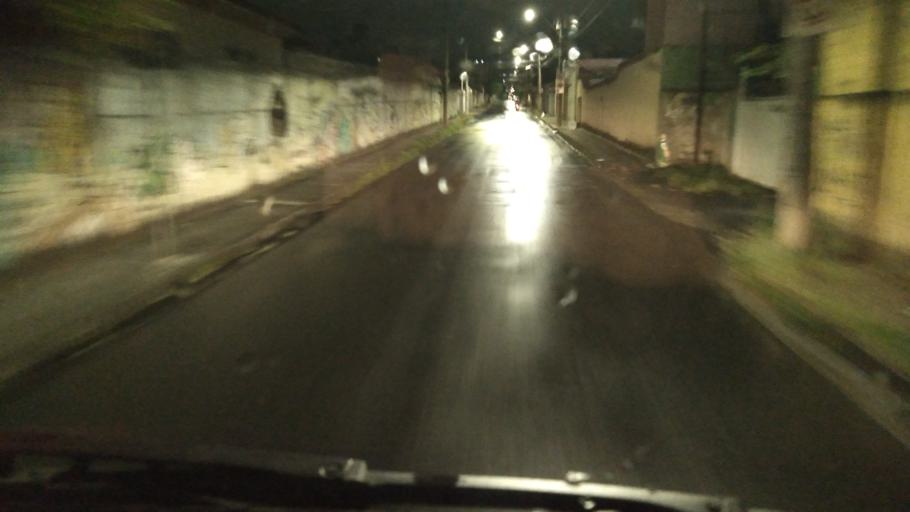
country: BR
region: Minas Gerais
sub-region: Belo Horizonte
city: Belo Horizonte
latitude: -19.8982
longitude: -43.9150
